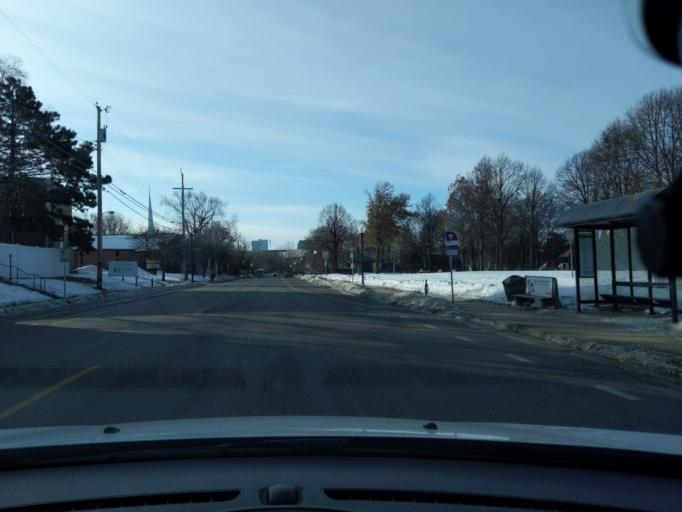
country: US
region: Minnesota
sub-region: Ramsey County
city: Lauderdale
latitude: 44.9877
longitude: -93.2304
